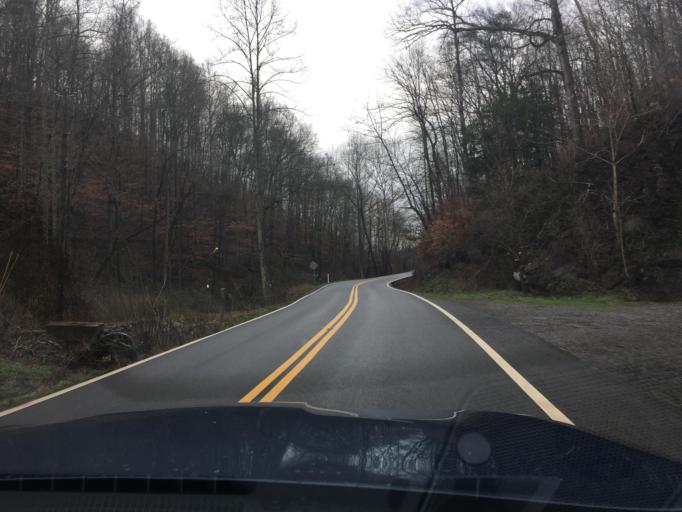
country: US
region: Tennessee
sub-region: McMinn County
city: Englewood
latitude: 35.3998
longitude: -84.4447
